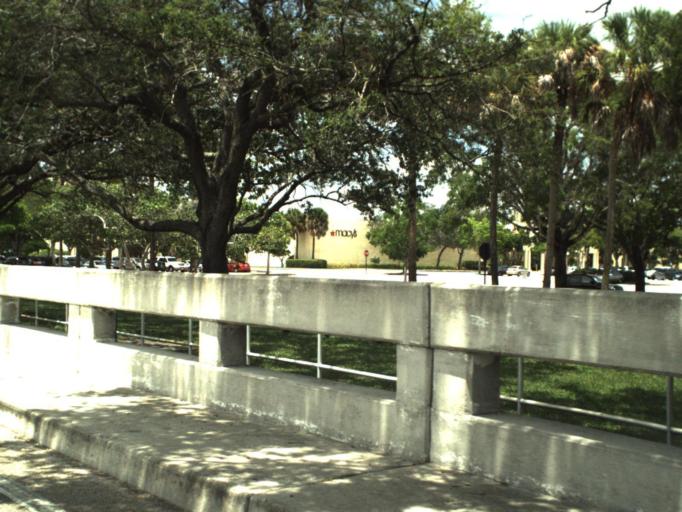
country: US
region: Florida
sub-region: Broward County
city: Tamarac
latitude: 26.2389
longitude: -80.2483
